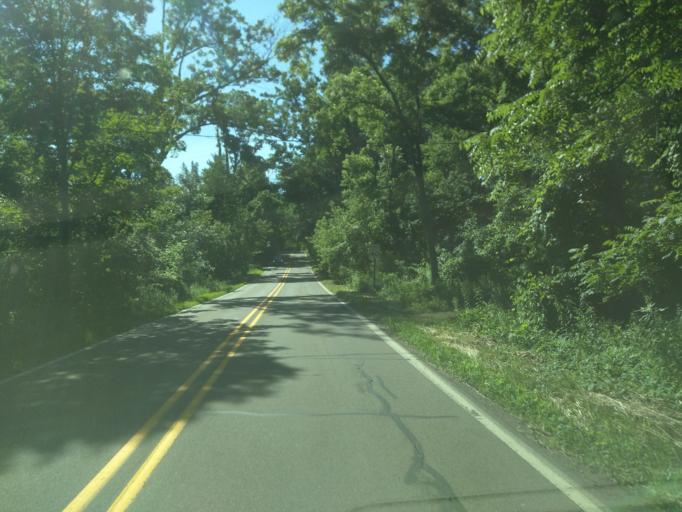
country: US
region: Michigan
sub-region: Ingham County
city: Edgemont Park
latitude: 42.7634
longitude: -84.6118
